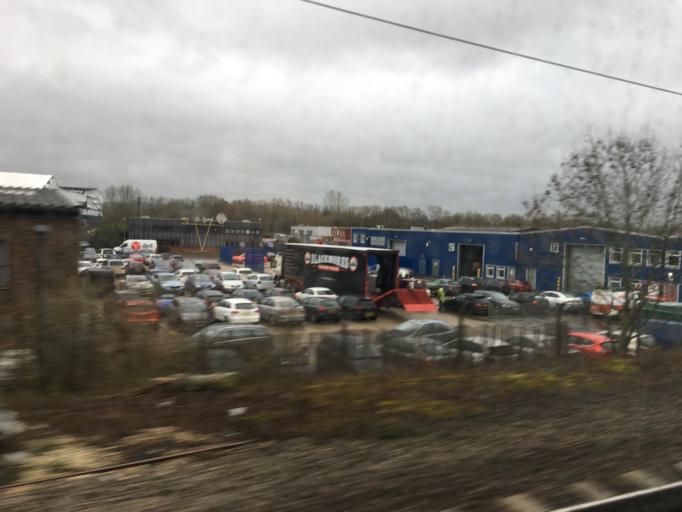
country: GB
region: England
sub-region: West Berkshire
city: Greenham
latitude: 51.3984
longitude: -1.2958
